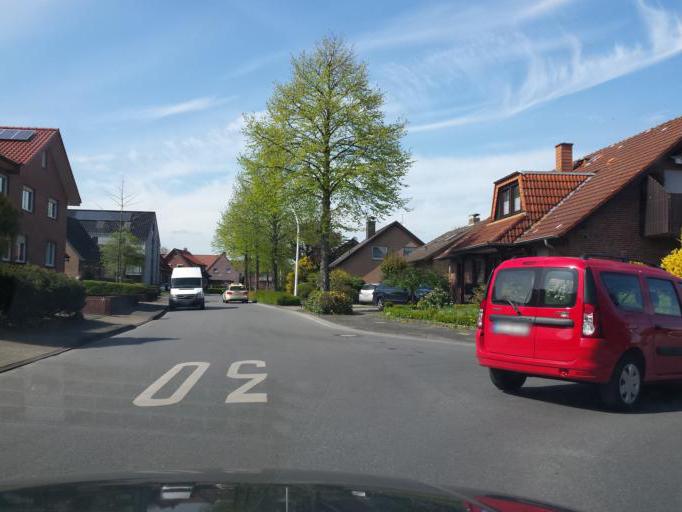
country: DE
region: North Rhine-Westphalia
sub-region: Regierungsbezirk Munster
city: Nottuln
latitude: 51.9224
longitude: 7.3590
